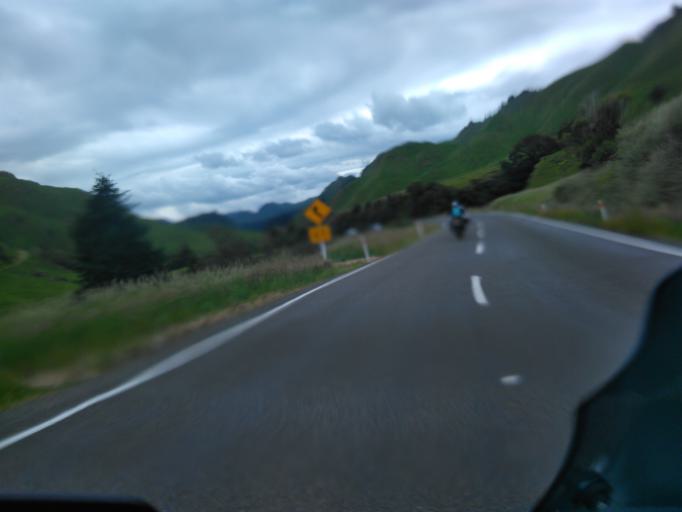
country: NZ
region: Bay of Plenty
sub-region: Opotiki District
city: Opotiki
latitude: -38.3657
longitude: 177.4628
